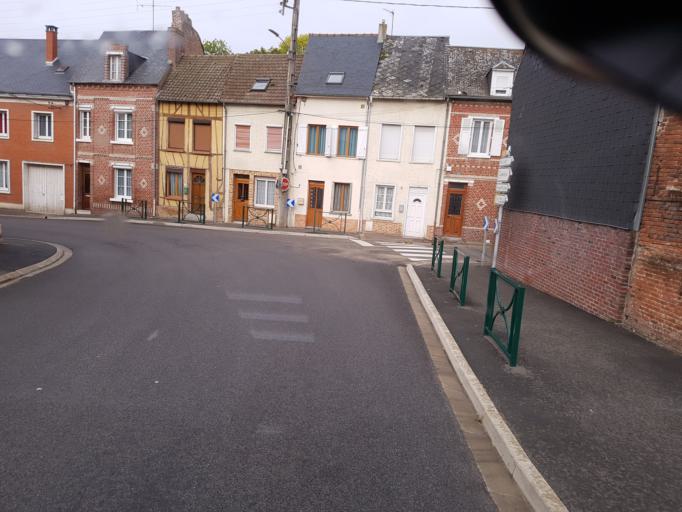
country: FR
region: Picardie
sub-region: Departement de l'Oise
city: Breteuil
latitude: 49.6354
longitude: 2.2956
